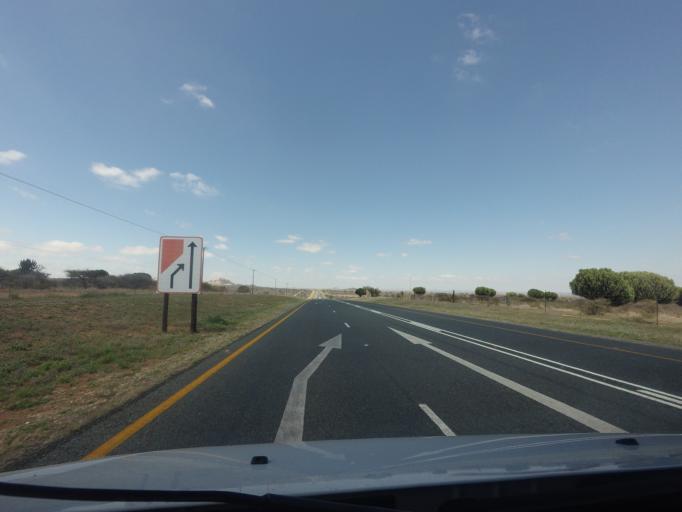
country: ZA
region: Limpopo
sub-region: Vhembe District Municipality
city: Louis Trichardt
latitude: -23.4049
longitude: 29.7577
